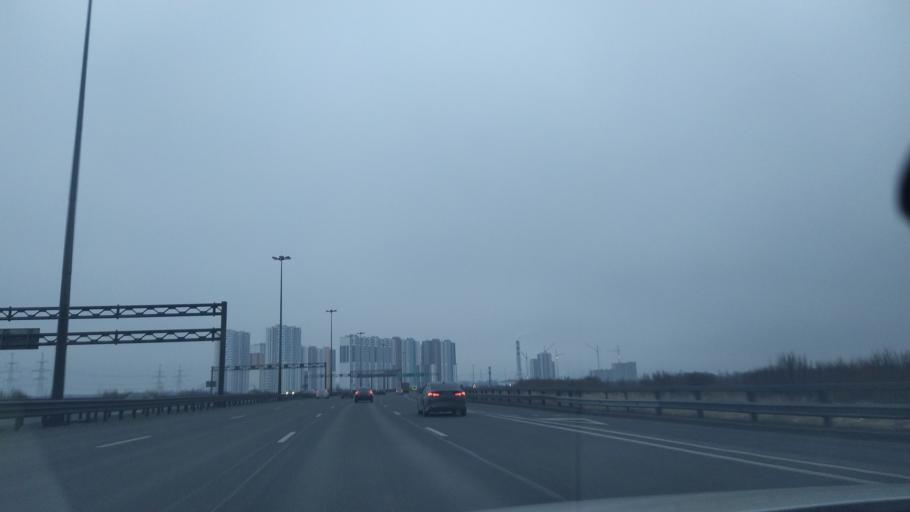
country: RU
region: Leningrad
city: Murino
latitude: 60.0153
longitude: 30.4668
